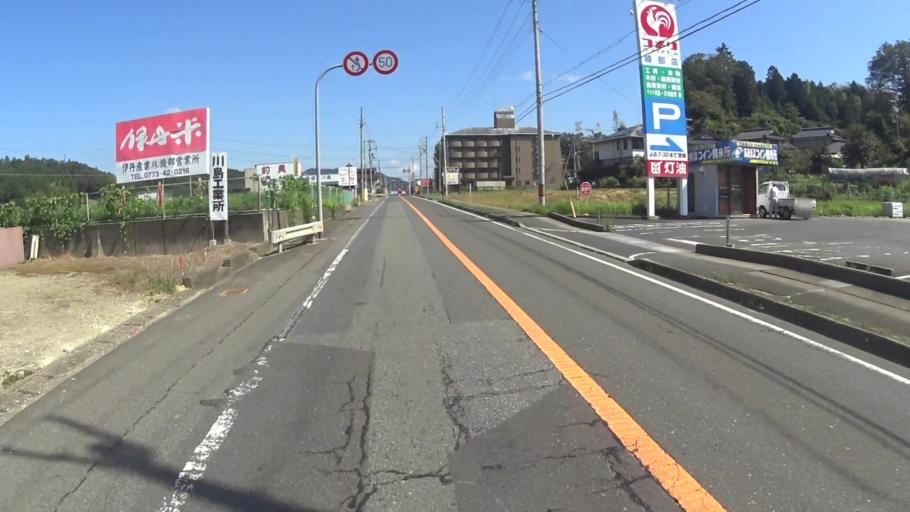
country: JP
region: Kyoto
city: Ayabe
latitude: 35.3148
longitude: 135.2834
